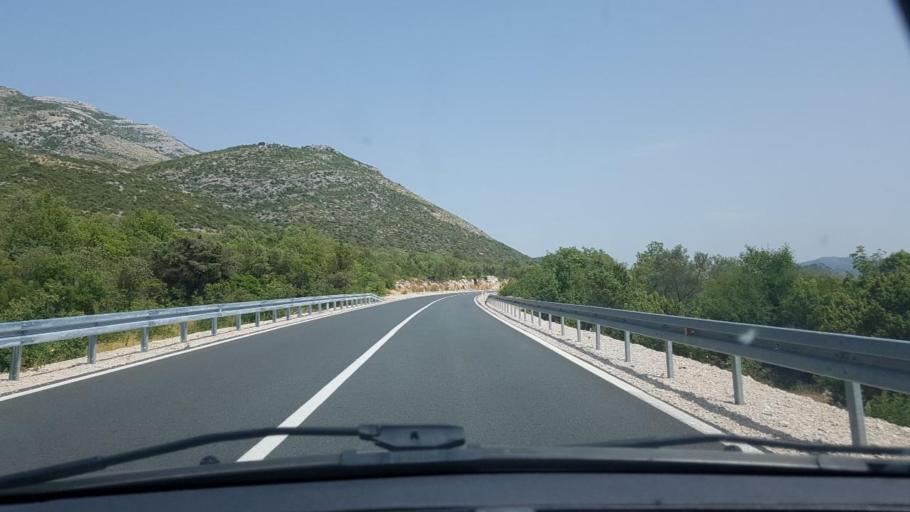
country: BA
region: Federation of Bosnia and Herzegovina
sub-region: Hercegovacko-Bosanski Kanton
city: Neum
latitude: 42.9589
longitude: 17.7176
